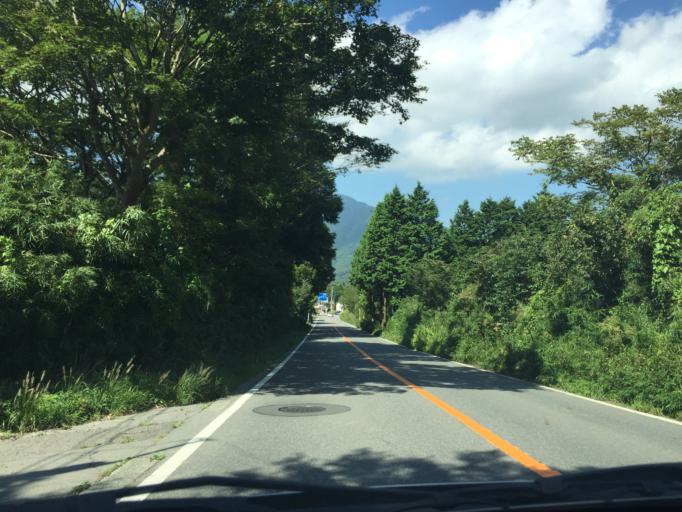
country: JP
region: Shizuoka
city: Gotemba
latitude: 35.2567
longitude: 139.0006
